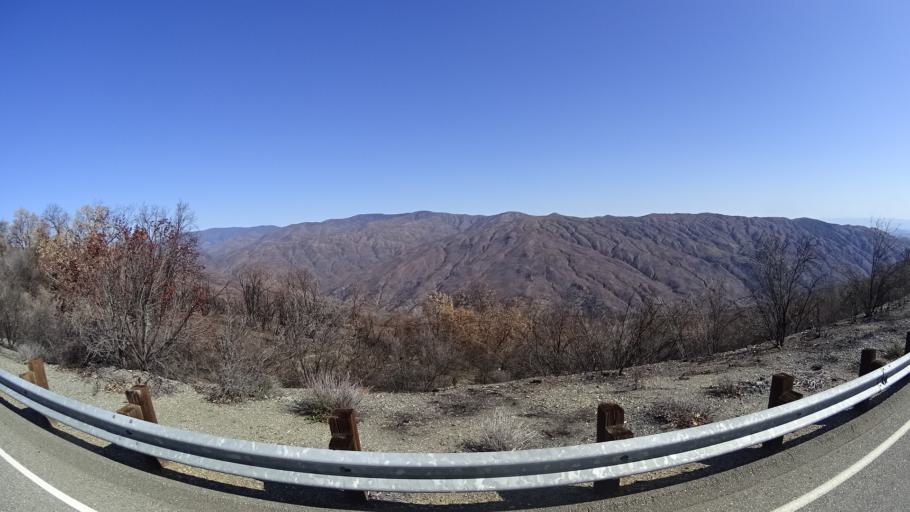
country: US
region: California
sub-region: Tehama County
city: Rancho Tehama Reserve
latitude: 39.6675
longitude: -122.6820
